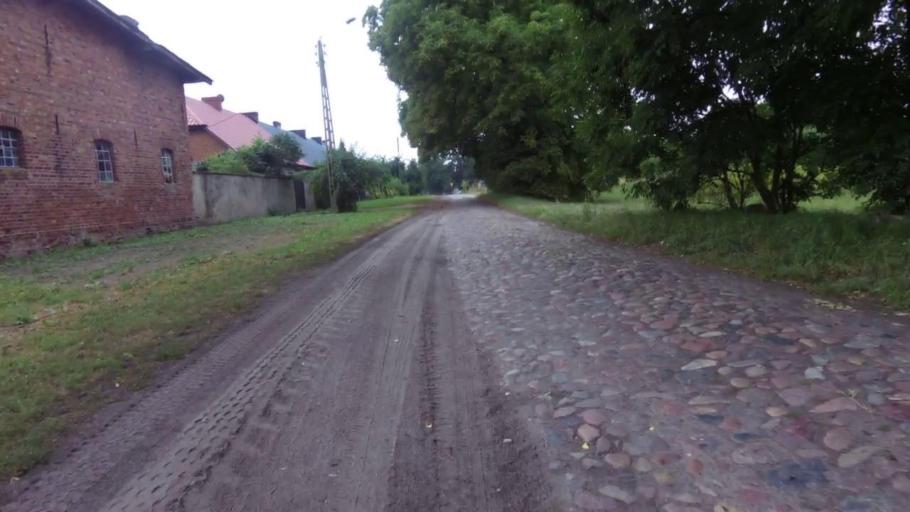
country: PL
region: West Pomeranian Voivodeship
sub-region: Powiat choszczenski
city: Choszczno
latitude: 53.2301
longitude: 15.3821
